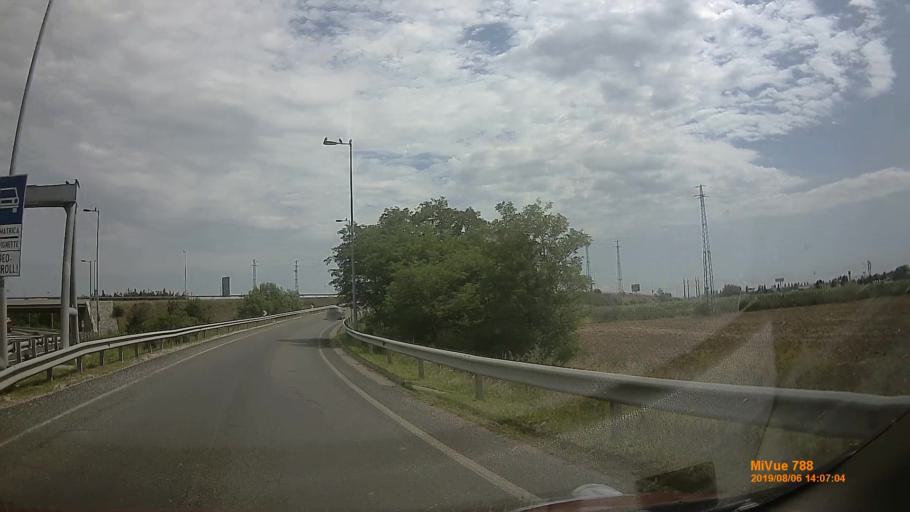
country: HU
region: Vas
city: Szombathely
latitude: 47.2481
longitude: 16.6529
